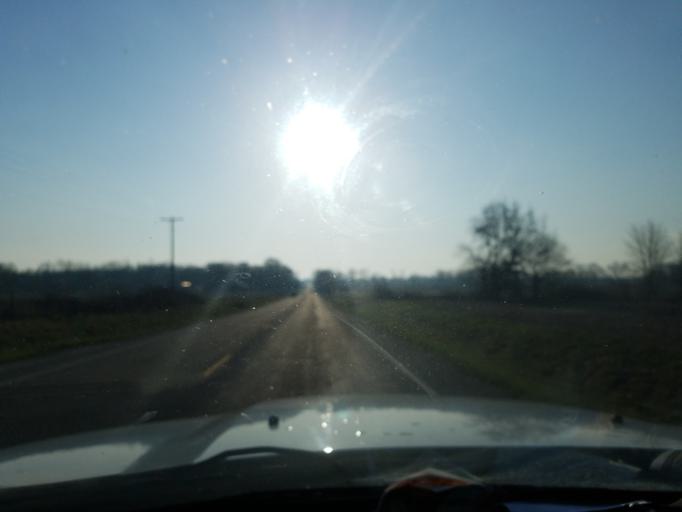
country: US
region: Indiana
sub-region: Vigo County
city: Seelyville
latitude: 39.3902
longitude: -87.2500
